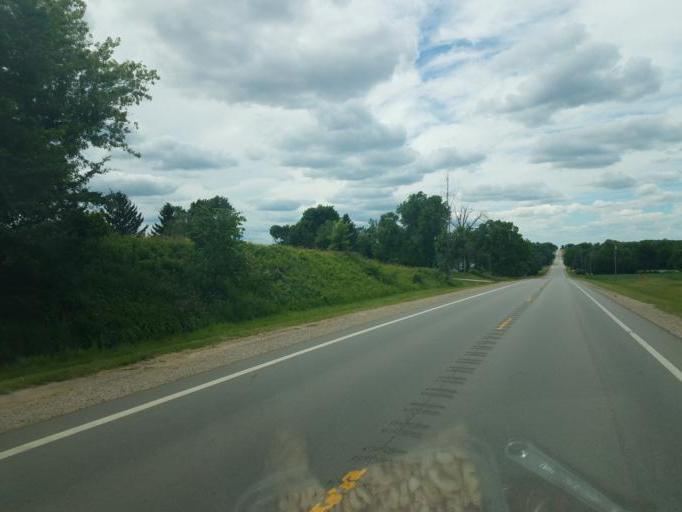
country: US
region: Michigan
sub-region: Eaton County
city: Charlotte
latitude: 42.6661
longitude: -84.9211
